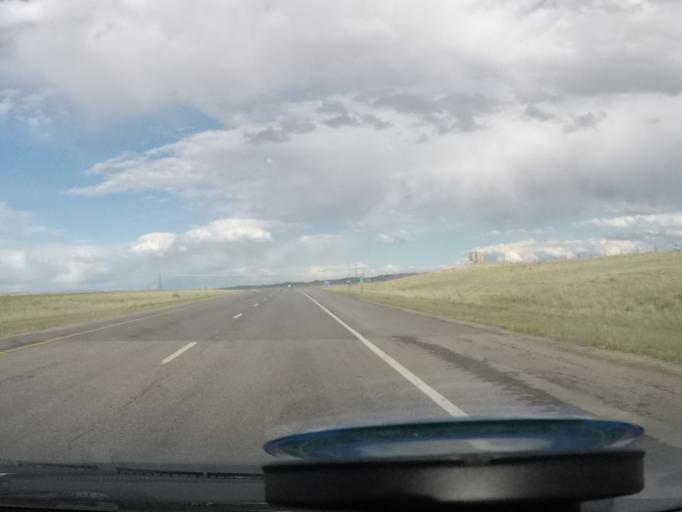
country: US
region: Wyoming
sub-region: Converse County
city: Glenrock
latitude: 42.8401
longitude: -106.0519
